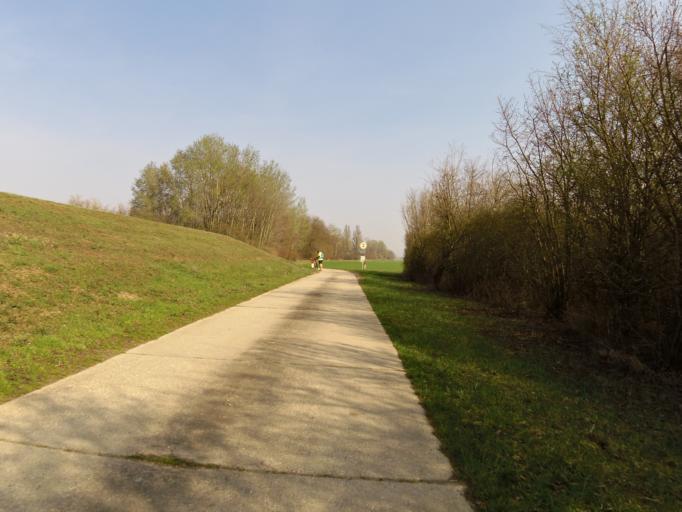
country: DE
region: Hesse
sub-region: Regierungsbezirk Darmstadt
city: Biblis
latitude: 49.7125
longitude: 8.4275
